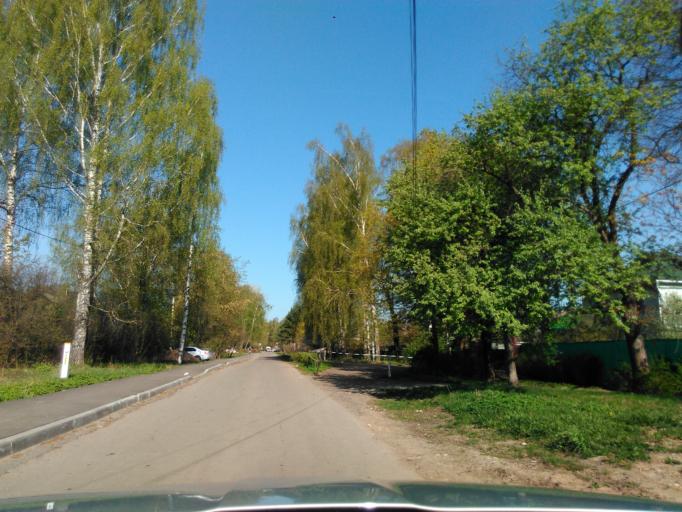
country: RU
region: Moskovskaya
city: Skhodnya
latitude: 55.9587
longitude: 37.2721
